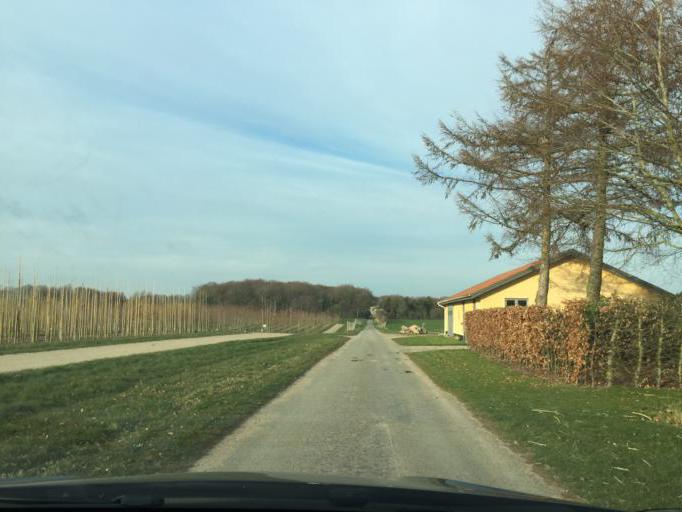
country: DK
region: South Denmark
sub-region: Kerteminde Kommune
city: Langeskov
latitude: 55.3296
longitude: 10.5848
